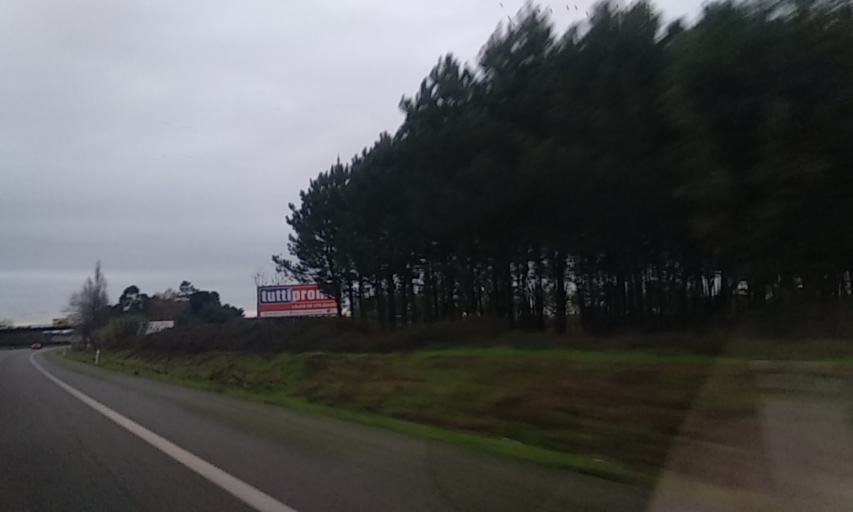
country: PT
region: Aveiro
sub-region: Anadia
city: Sangalhos
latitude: 40.4406
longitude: -8.5142
